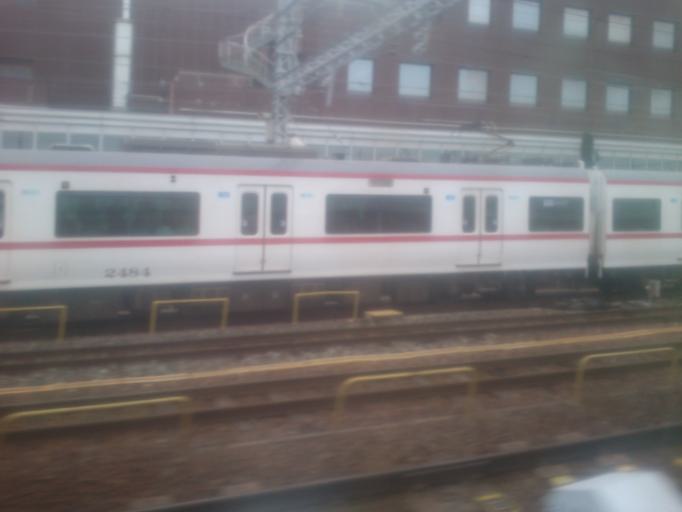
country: JP
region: Aichi
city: Nagoya-shi
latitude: 35.1856
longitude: 136.8711
